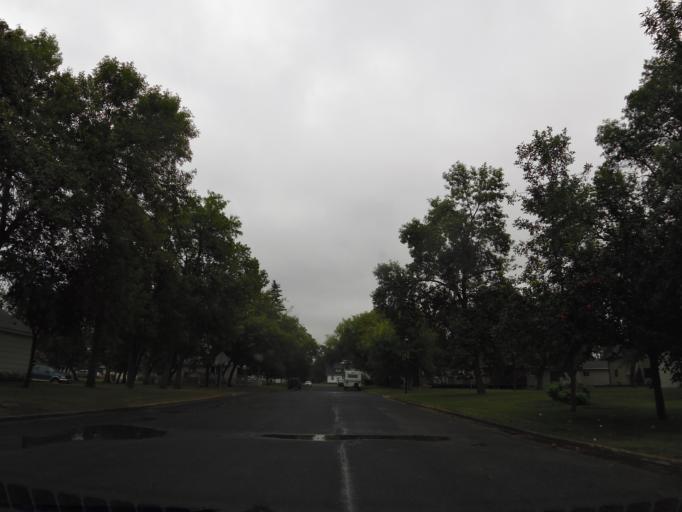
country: US
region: Minnesota
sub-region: Marshall County
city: Warren
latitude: 48.1971
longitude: -96.7644
